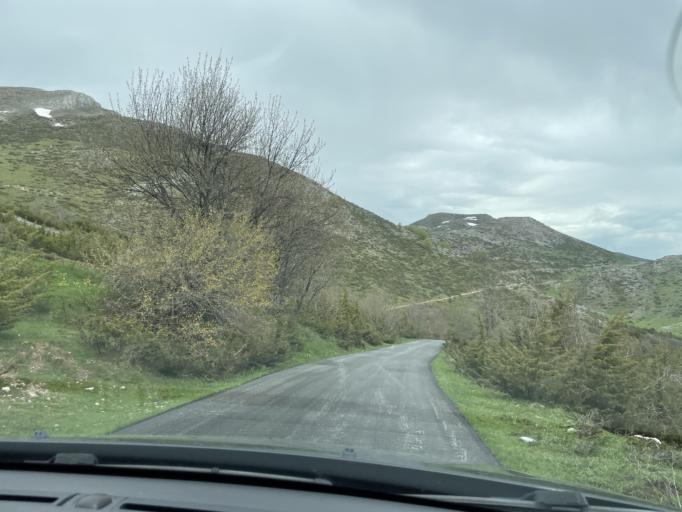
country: MK
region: Opstina Rostusa
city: Rostusha
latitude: 41.6245
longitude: 20.6832
